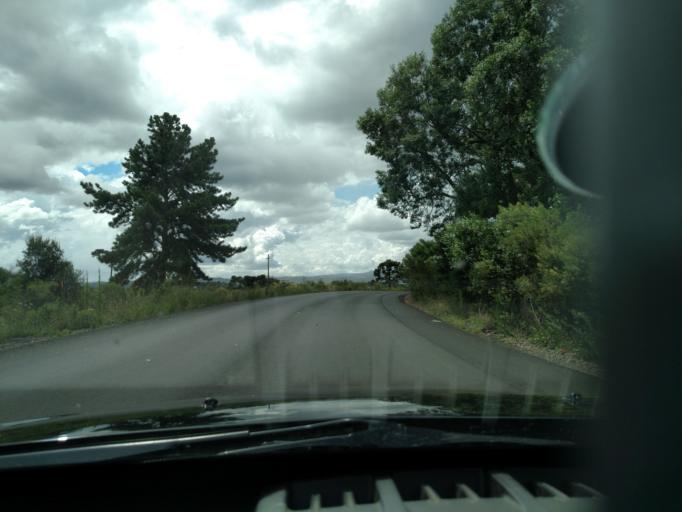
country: BR
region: Santa Catarina
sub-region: Sao Joaquim
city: Sao Joaquim
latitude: -28.1200
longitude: -50.0515
